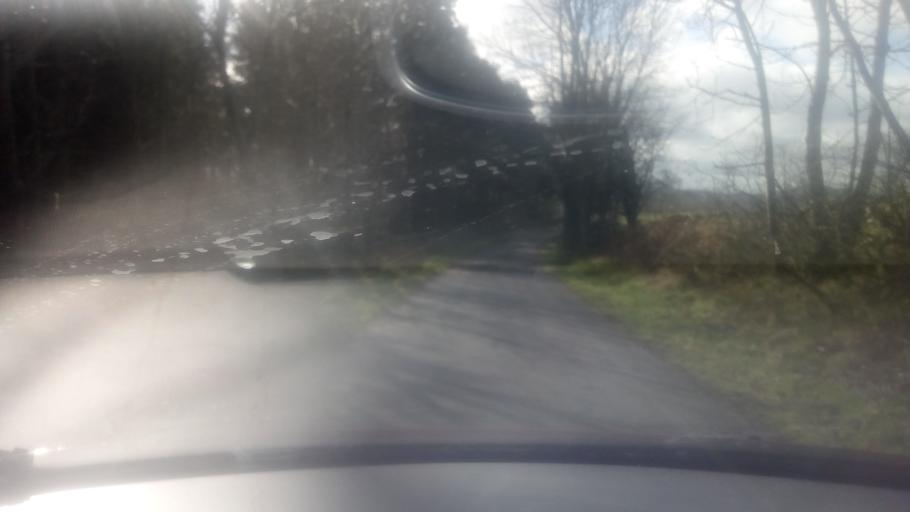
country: GB
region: Scotland
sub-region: The Scottish Borders
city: Jedburgh
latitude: 55.5252
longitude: -2.5747
